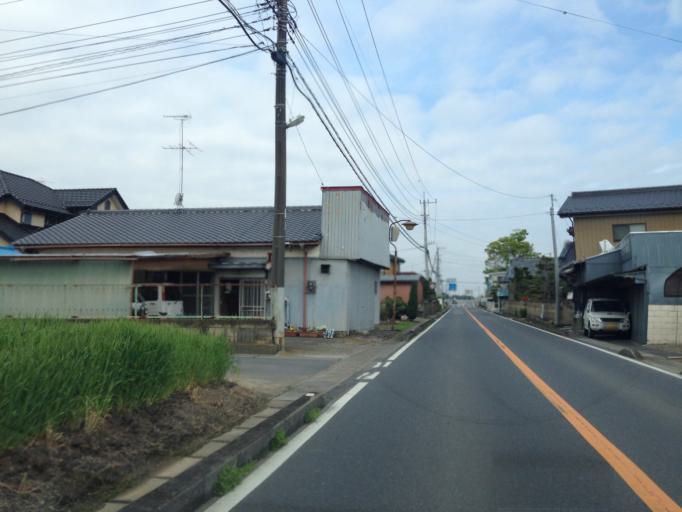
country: JP
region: Ibaraki
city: Ishige
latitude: 36.1493
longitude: 139.9957
